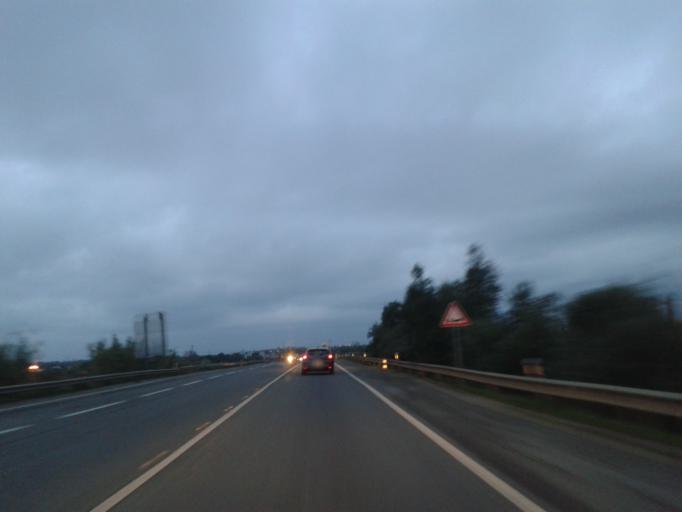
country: PT
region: Faro
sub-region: Albufeira
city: Ferreiras
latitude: 37.1237
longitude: -8.2524
